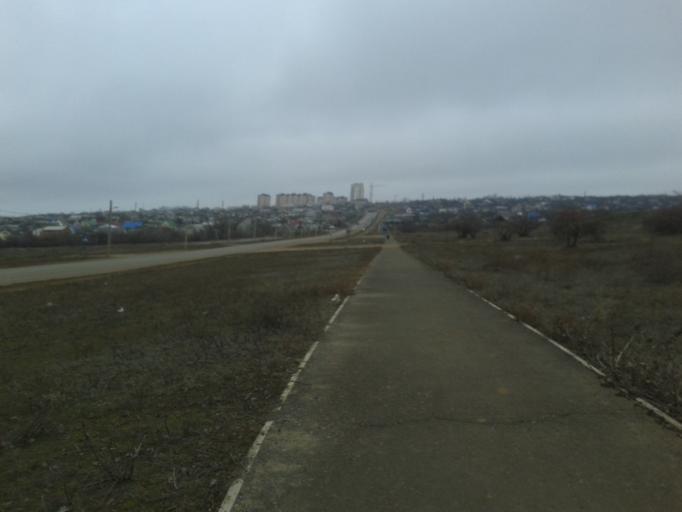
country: RU
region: Volgograd
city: Volgograd
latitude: 48.6584
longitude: 44.4141
